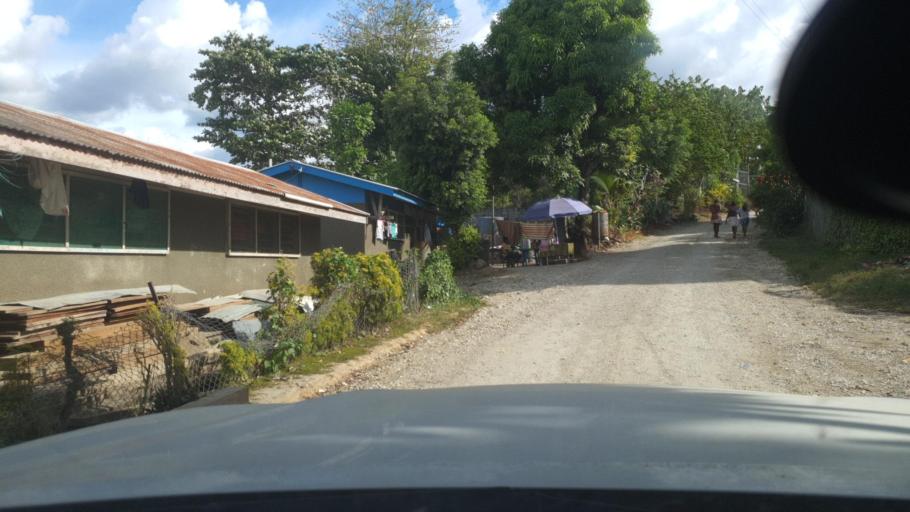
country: SB
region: Guadalcanal
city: Honiara
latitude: -9.4365
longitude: 159.9474
